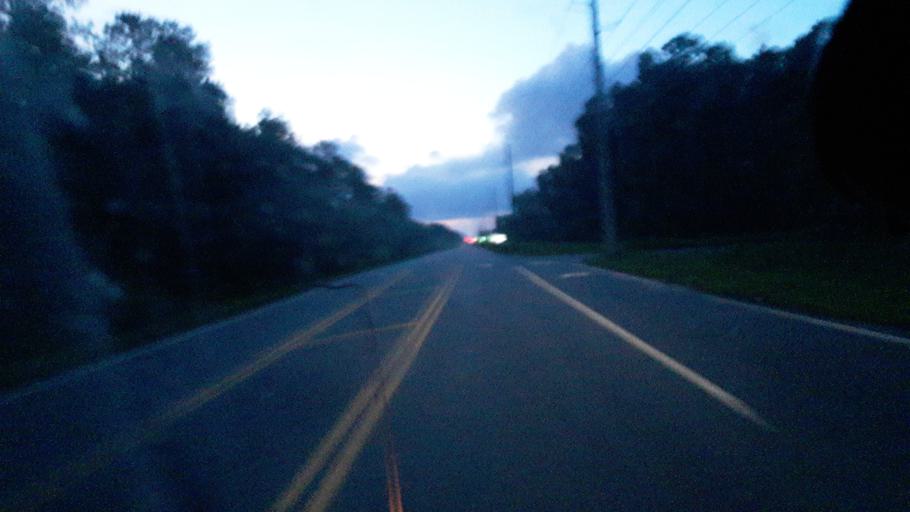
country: US
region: North Carolina
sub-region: Brunswick County
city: Oak Island
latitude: 33.9891
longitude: -78.2021
